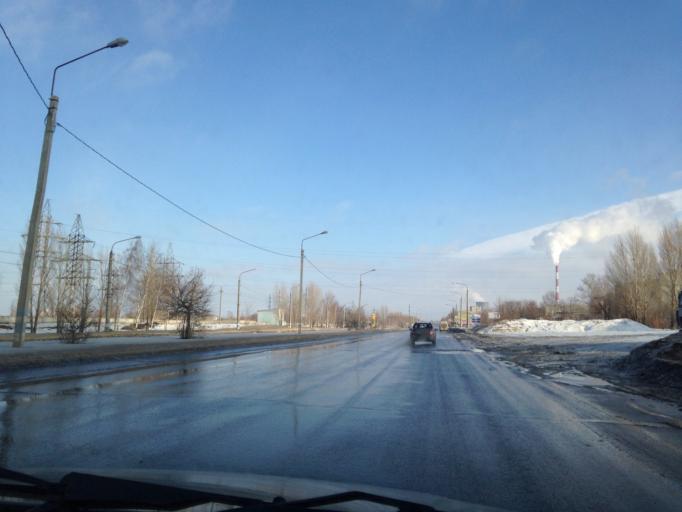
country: RU
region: Ulyanovsk
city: Mirnyy
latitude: 54.3481
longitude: 48.5788
